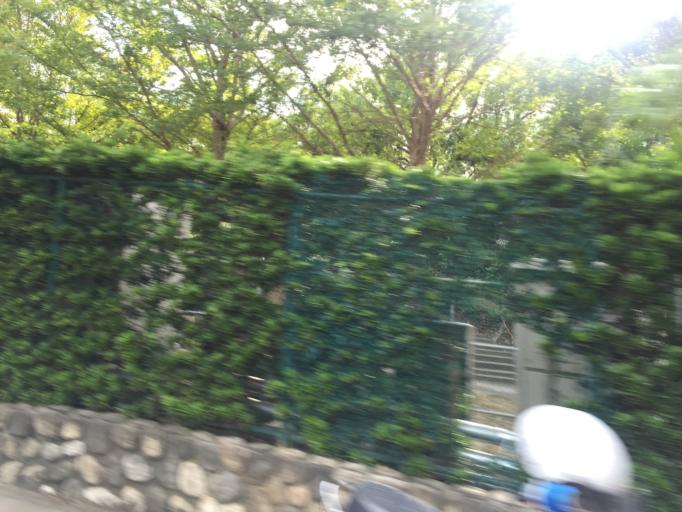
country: TW
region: Taiwan
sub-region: Hsinchu
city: Hsinchu
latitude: 24.7777
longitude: 120.9410
